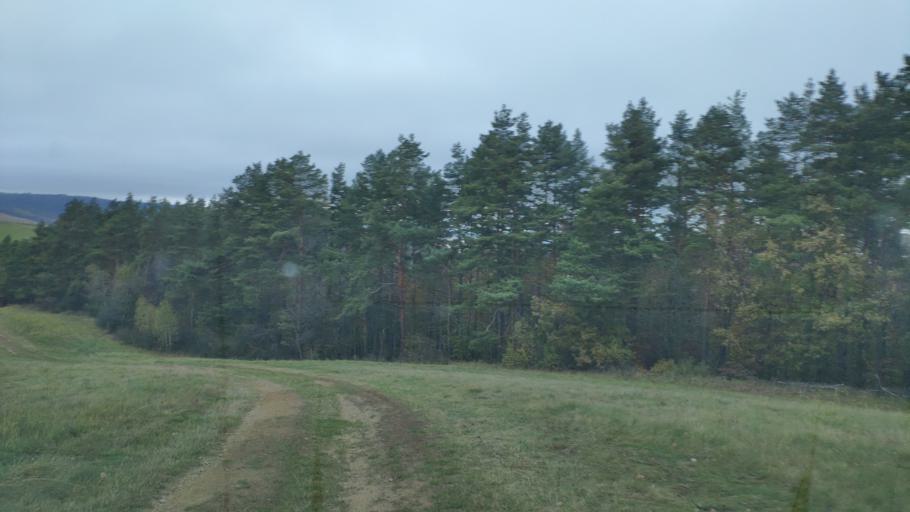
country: SK
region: Presovsky
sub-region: Okres Presov
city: Presov
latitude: 48.9352
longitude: 21.1096
